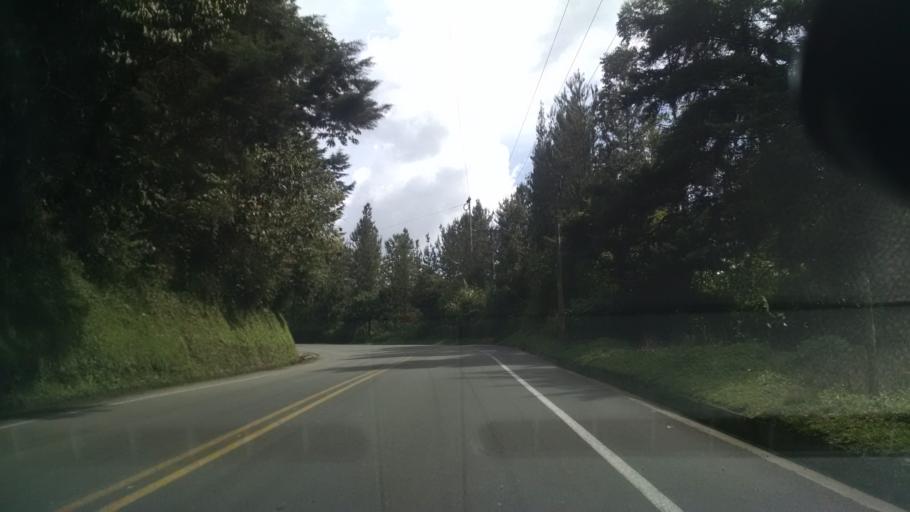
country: CO
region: Antioquia
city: Caldas
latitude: 6.0424
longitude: -75.6295
